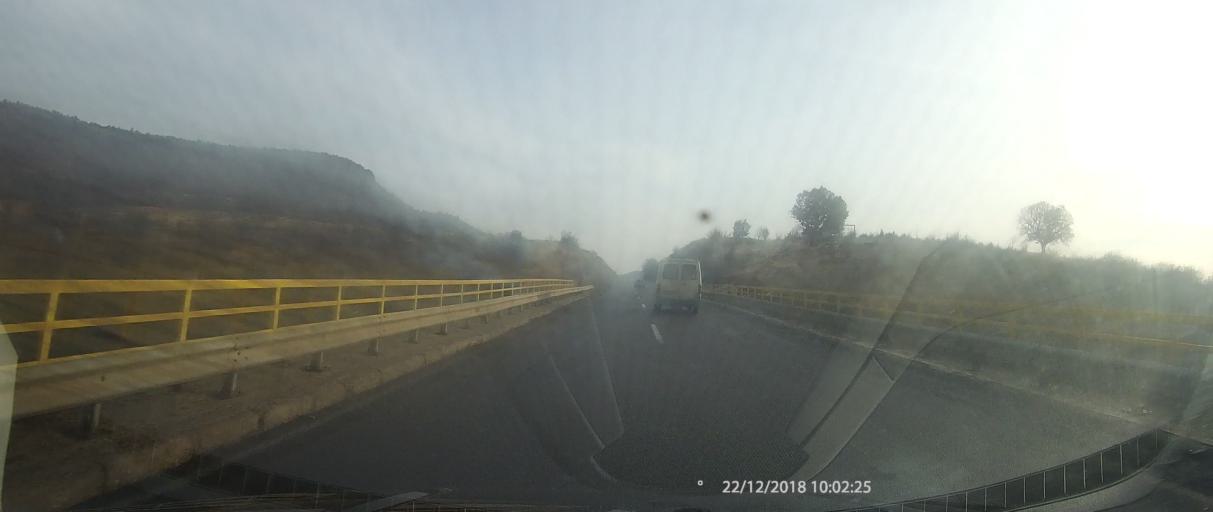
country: MK
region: Opstina Rankovce
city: Rankovce
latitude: 42.1471
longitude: 22.0124
